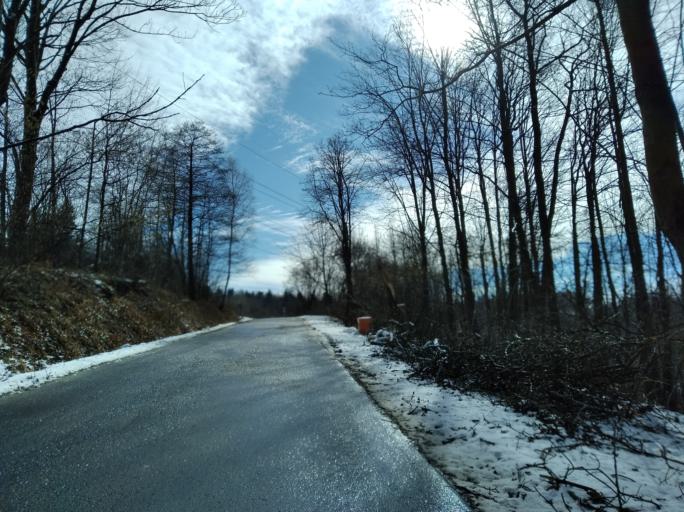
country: PL
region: Subcarpathian Voivodeship
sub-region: Powiat brzozowski
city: Jablonica Polska
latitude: 49.7315
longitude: 21.8951
